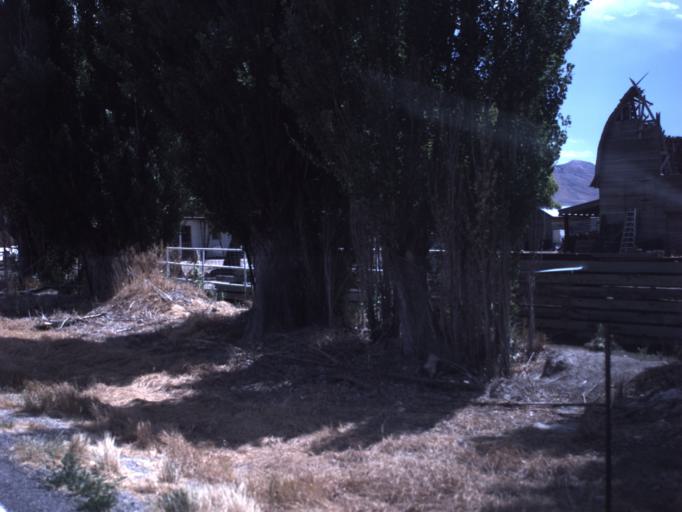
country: US
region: Utah
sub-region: Box Elder County
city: Tremonton
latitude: 41.6507
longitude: -112.3075
